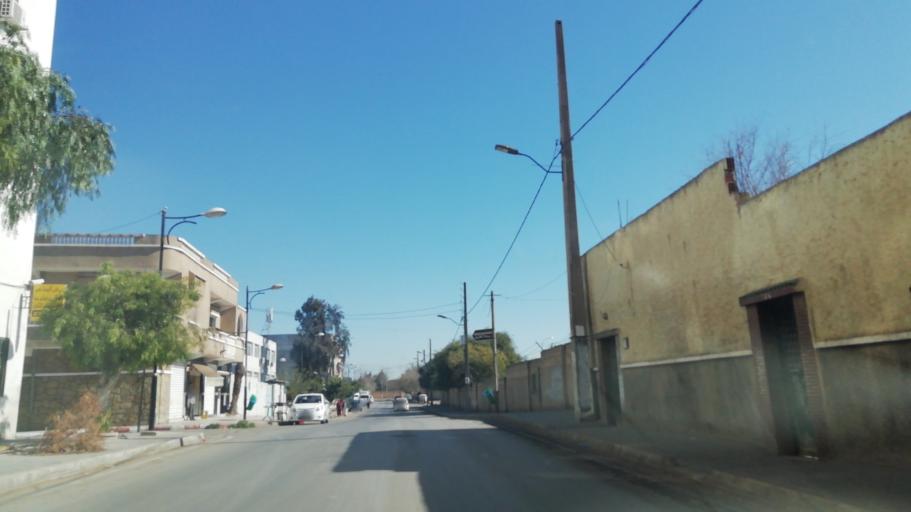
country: DZ
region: Oran
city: Es Senia
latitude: 35.6538
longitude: -0.6179
